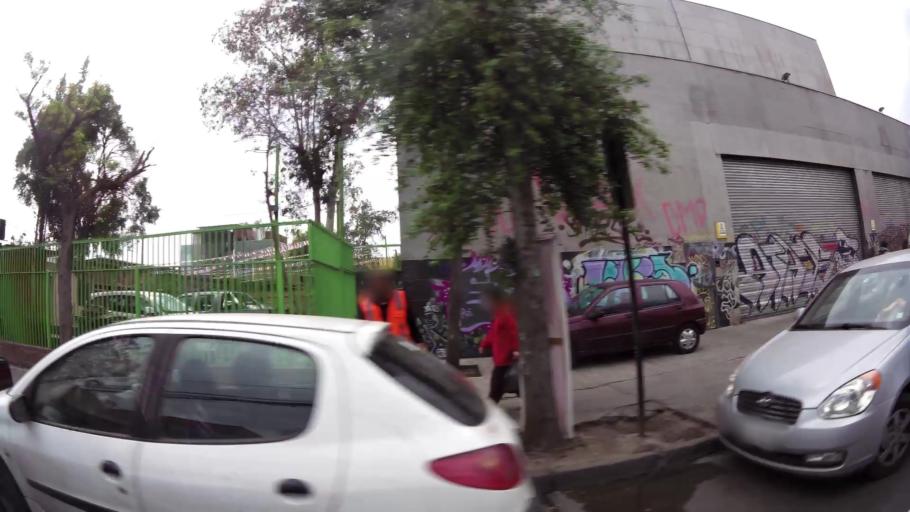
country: CL
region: Santiago Metropolitan
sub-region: Provincia de Santiago
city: Lo Prado
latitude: -33.5117
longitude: -70.7592
